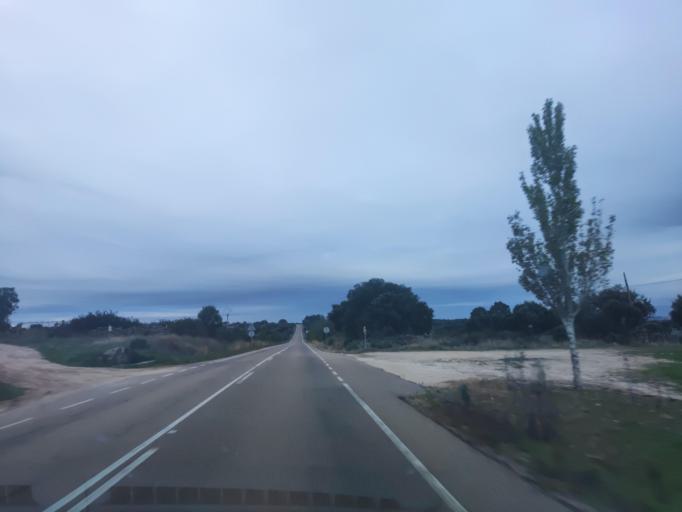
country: ES
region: Castille and Leon
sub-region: Provincia de Salamanca
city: Lumbrales
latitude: 40.9416
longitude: -6.7458
